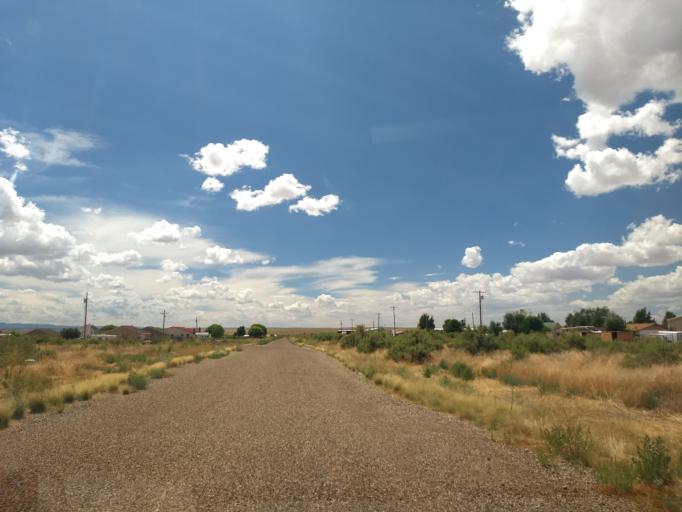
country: US
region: Arizona
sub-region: Coconino County
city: Fredonia
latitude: 36.9432
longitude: -112.5193
